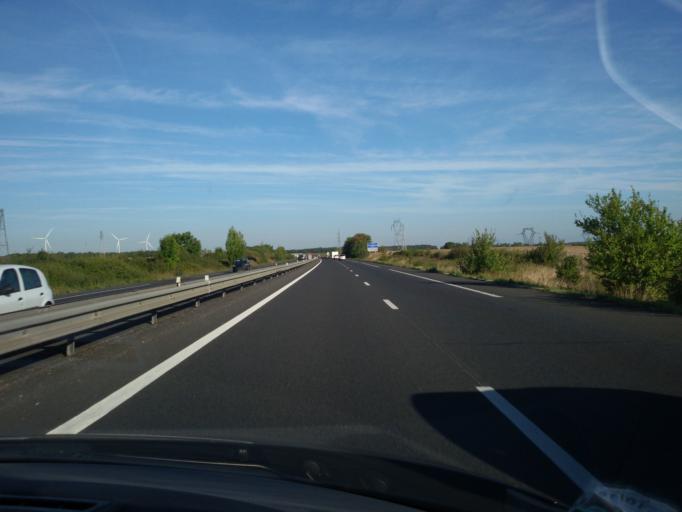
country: FR
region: Centre
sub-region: Departement du Cher
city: Marmagne
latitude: 47.0855
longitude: 2.2614
